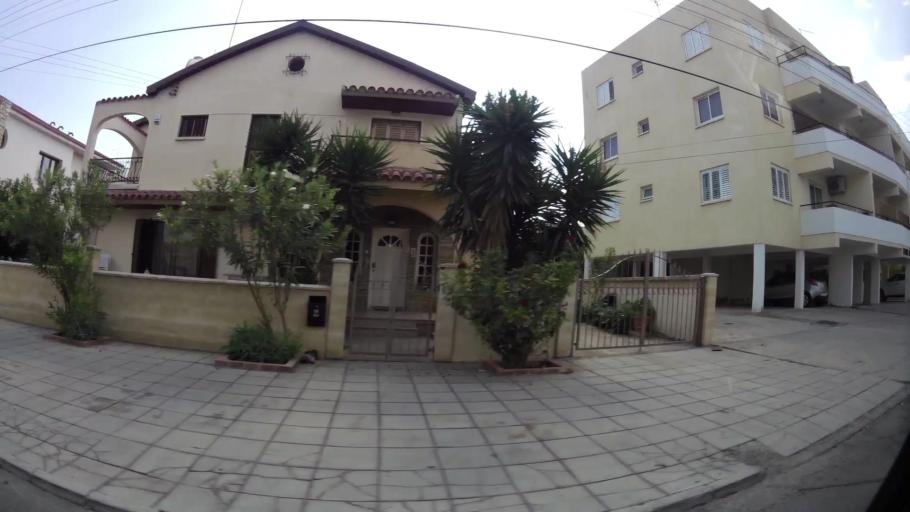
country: CY
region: Larnaka
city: Larnaca
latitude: 34.9140
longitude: 33.6119
